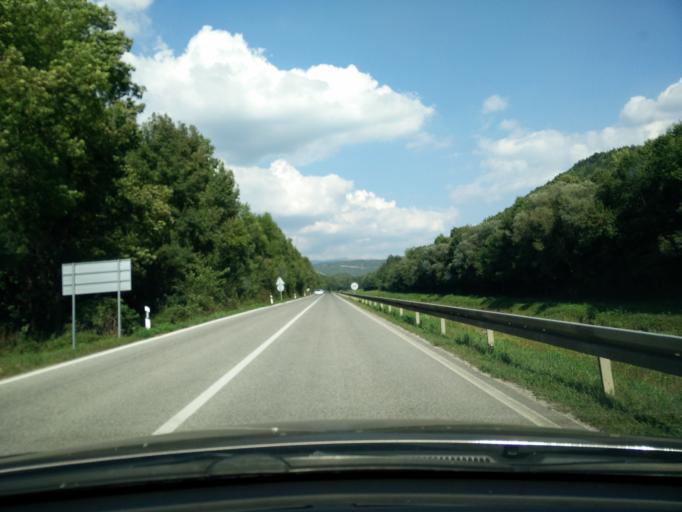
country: HR
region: Istarska
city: Karojba
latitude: 45.3593
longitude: 13.8600
